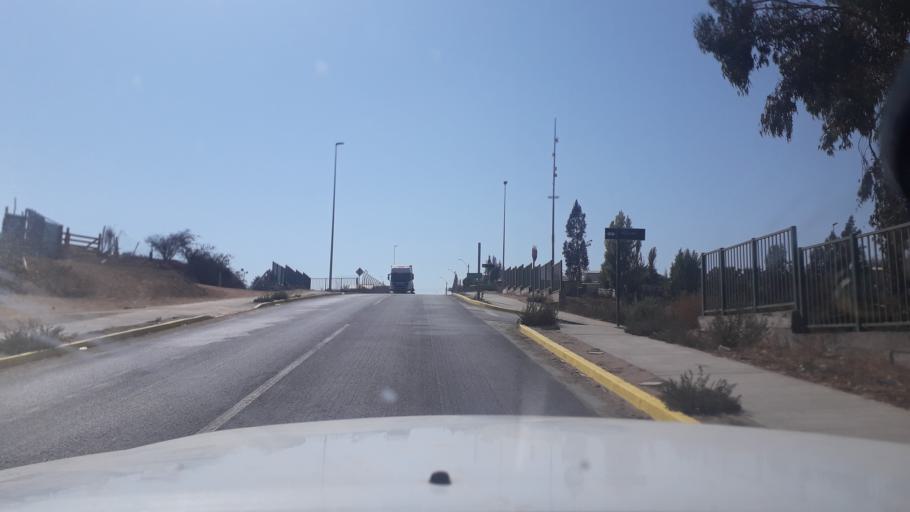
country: CL
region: Valparaiso
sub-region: Provincia de Marga Marga
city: Villa Alemana
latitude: -33.0667
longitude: -71.4034
